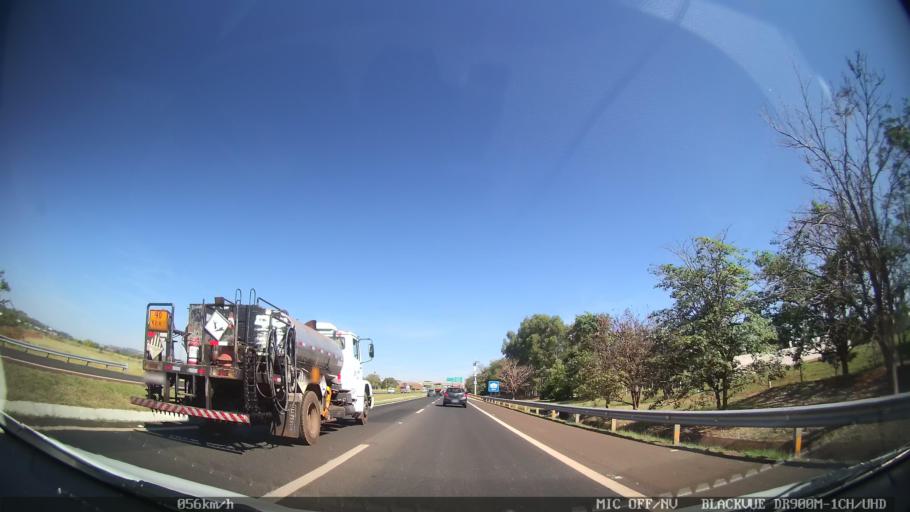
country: BR
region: Sao Paulo
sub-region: Ribeirao Preto
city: Ribeirao Preto
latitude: -21.2179
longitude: -47.7744
